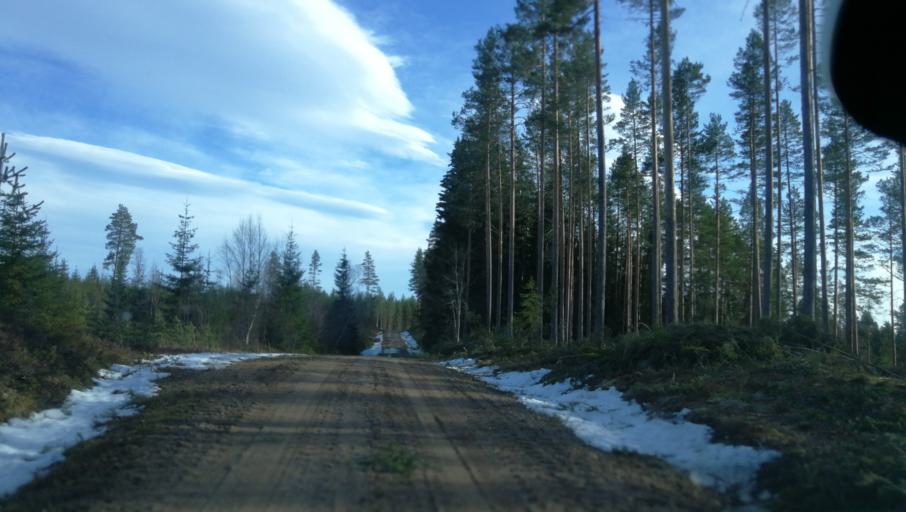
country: SE
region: Dalarna
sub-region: Vansbro Kommun
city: Vansbro
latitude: 60.8112
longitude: 14.2049
